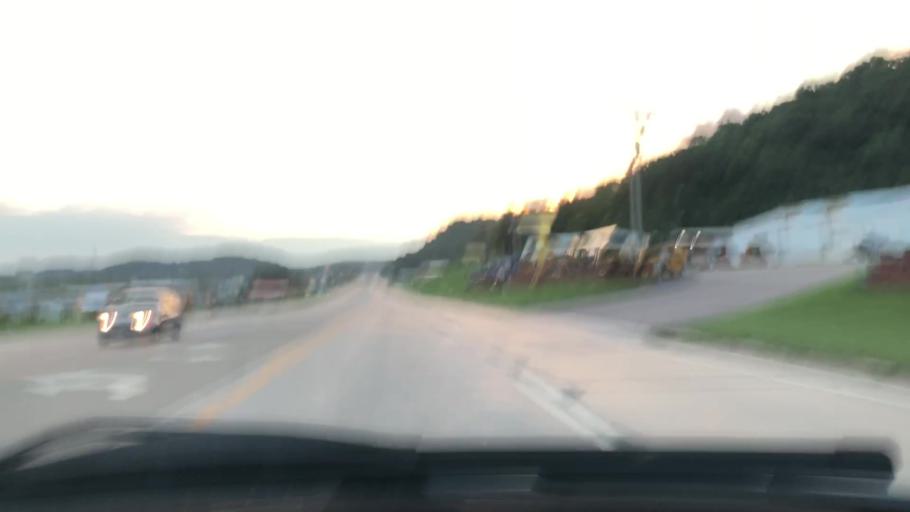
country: US
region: Wisconsin
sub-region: Richland County
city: Richland Center
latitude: 43.3188
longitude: -90.3634
